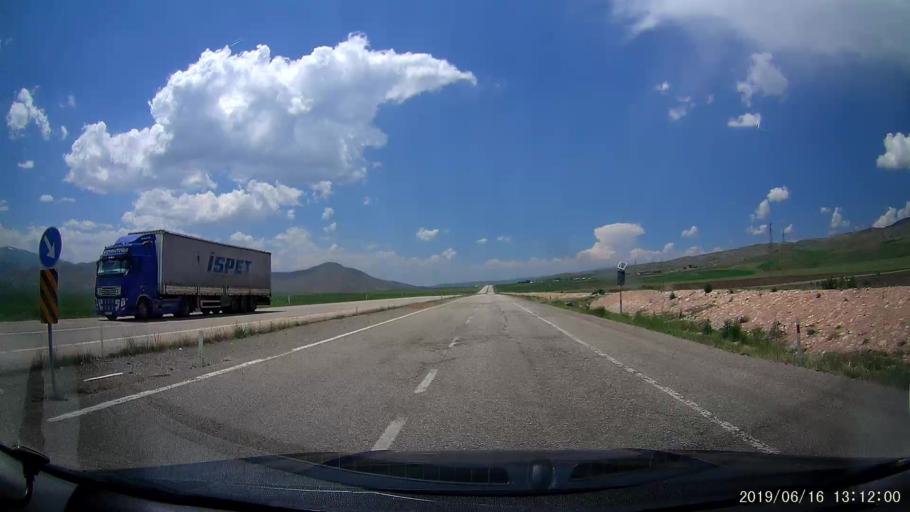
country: TR
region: Agri
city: Diyadin
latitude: 39.5961
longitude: 43.5914
